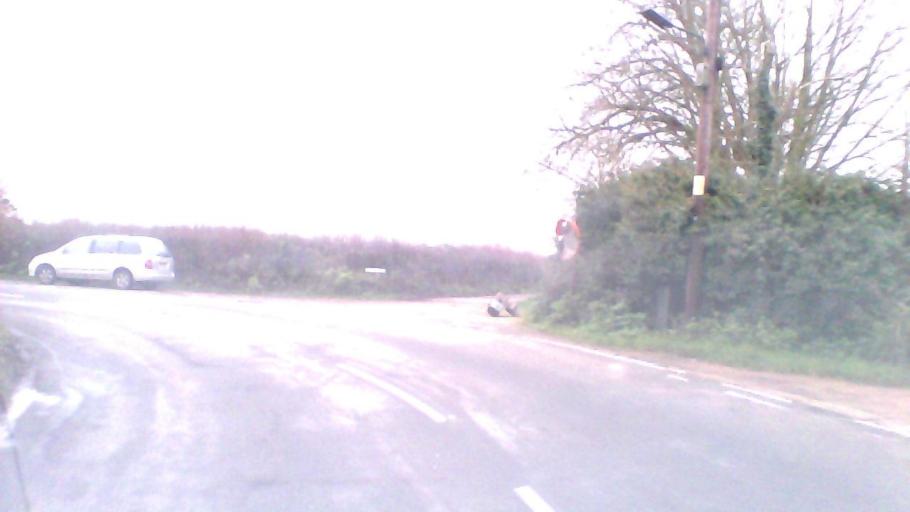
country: GB
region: England
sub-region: Isle of Wight
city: Bembridge
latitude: 50.6844
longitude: -1.0945
